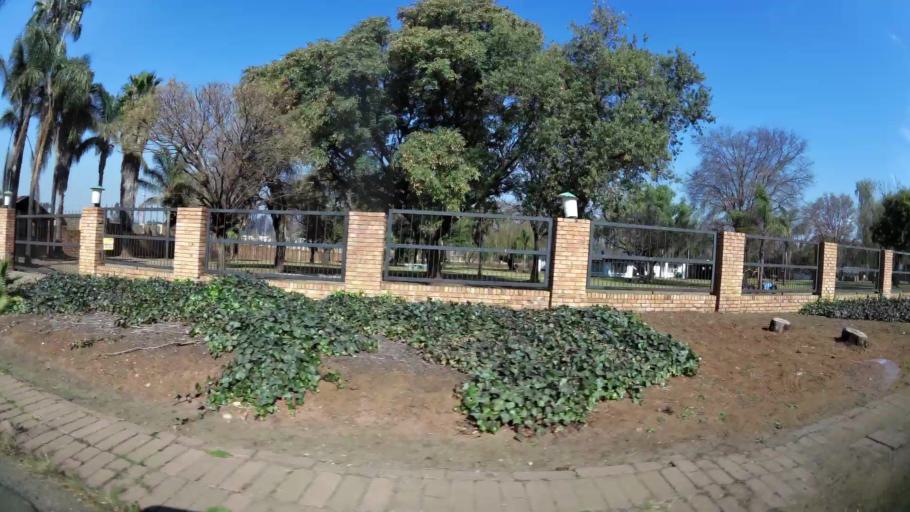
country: ZA
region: Gauteng
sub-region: Ekurhuleni Metropolitan Municipality
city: Boksburg
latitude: -26.1696
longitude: 28.2606
